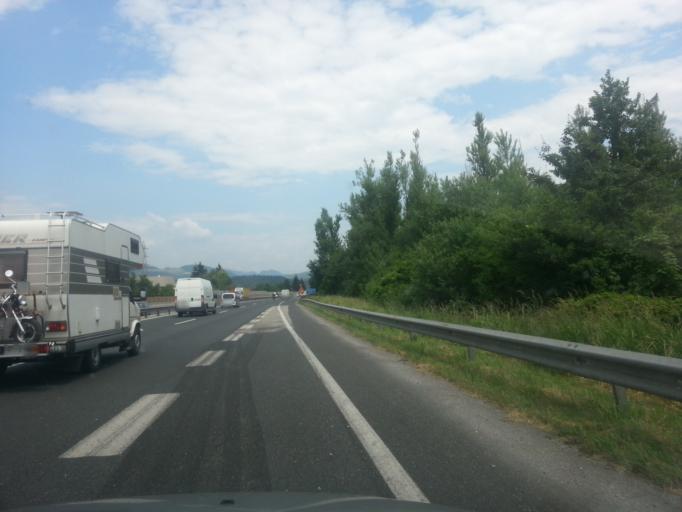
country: SI
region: Vrhnika
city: Vrhnika
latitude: 45.9696
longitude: 14.3051
